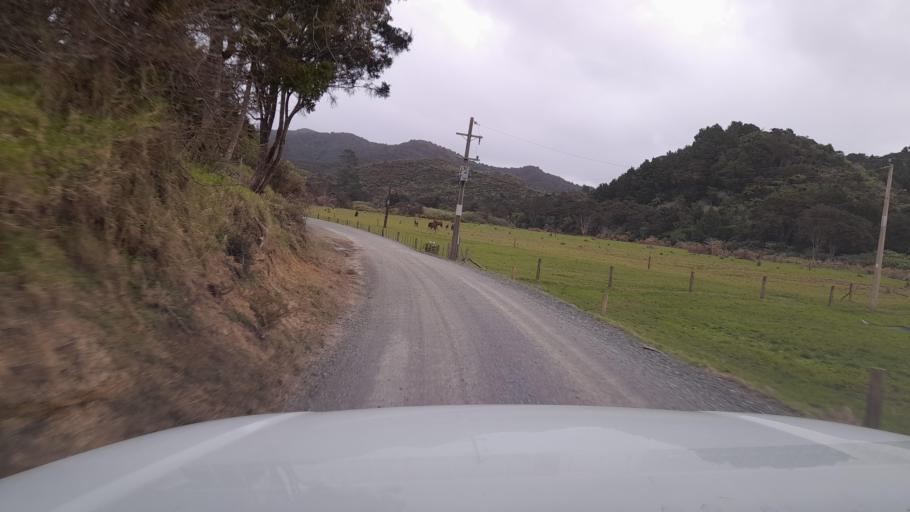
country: NZ
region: Northland
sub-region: Far North District
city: Paihia
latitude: -35.3457
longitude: 174.2278
